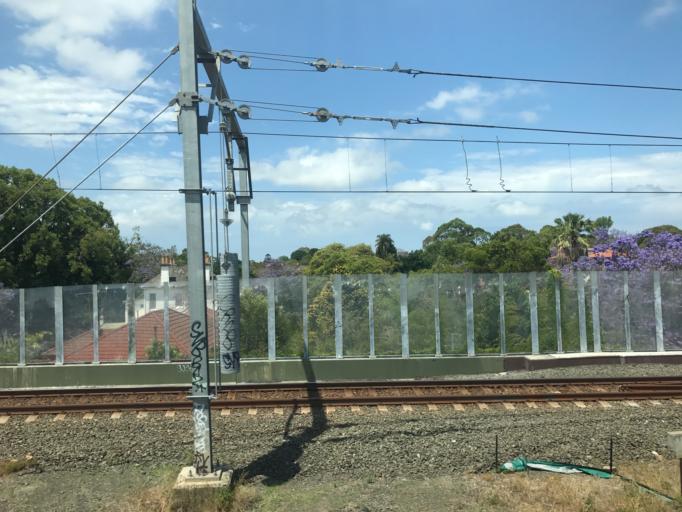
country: AU
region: New South Wales
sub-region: Willoughby
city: Chatswood
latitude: -33.7887
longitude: 151.1808
